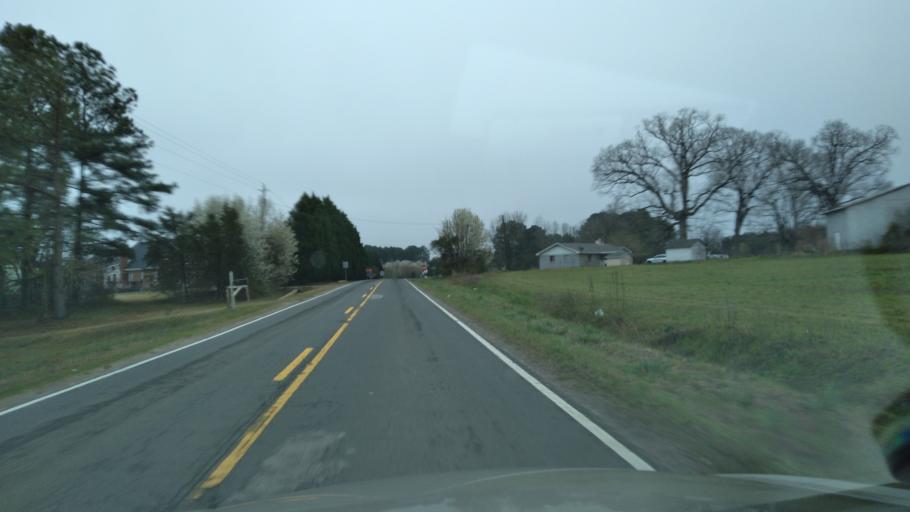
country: US
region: North Carolina
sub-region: Wake County
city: Knightdale
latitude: 35.7436
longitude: -78.4839
